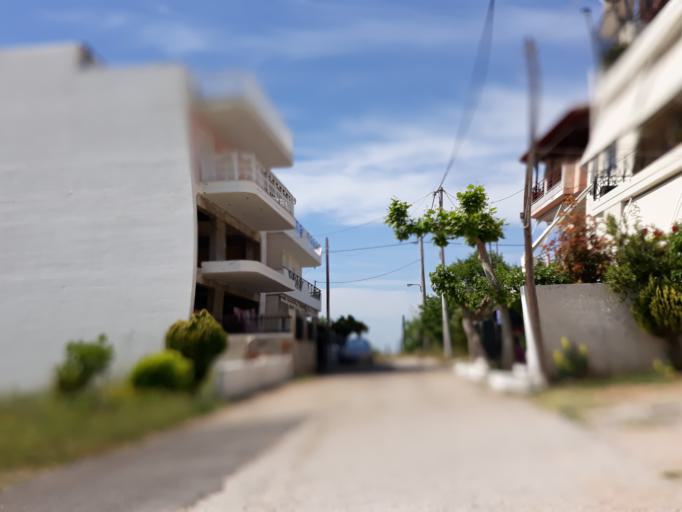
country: GR
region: Attica
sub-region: Nomarchia Dytikis Attikis
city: Ano Liosia
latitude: 38.0960
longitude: 23.6972
